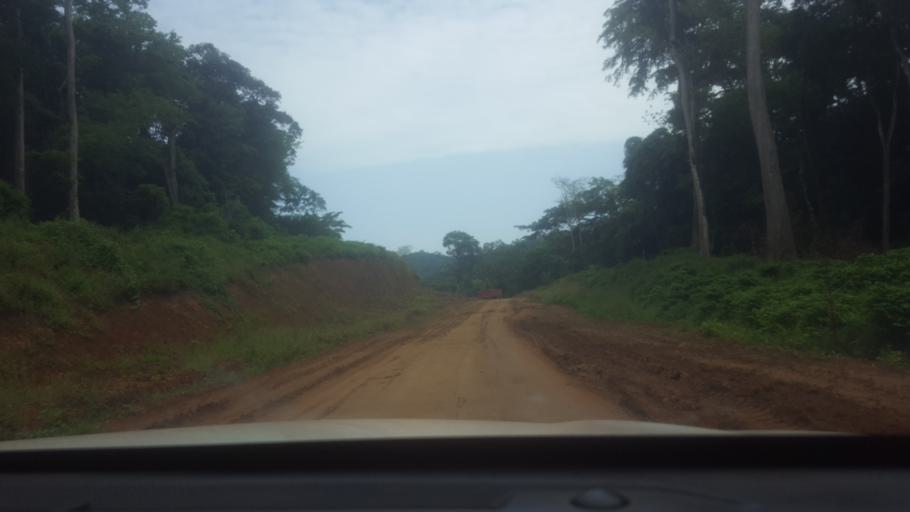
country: ET
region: Southern Nations, Nationalities, and People's Region
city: Tippi
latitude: 7.5228
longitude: 34.9925
